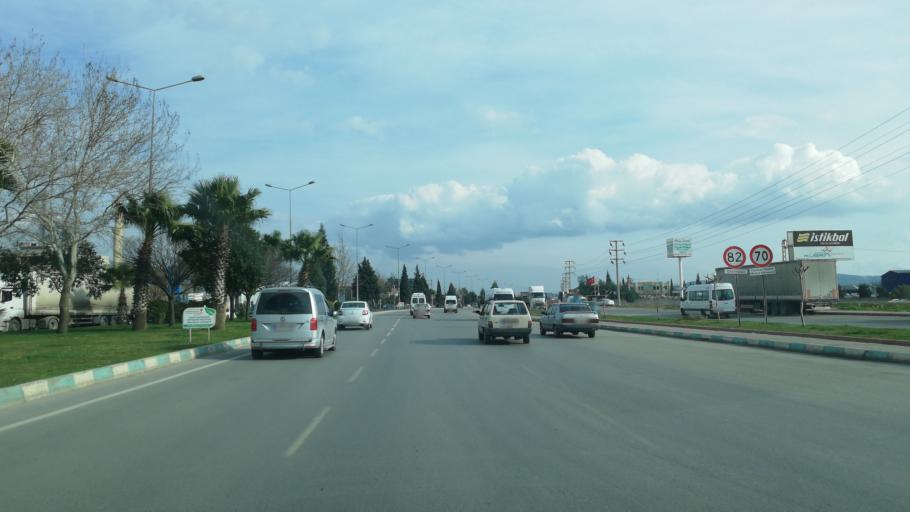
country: TR
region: Kahramanmaras
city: Kahramanmaras
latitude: 37.5579
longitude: 36.9559
